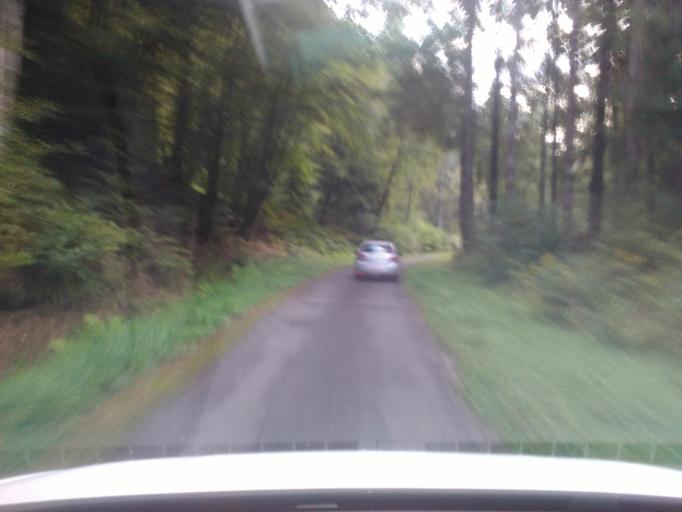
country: FR
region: Lorraine
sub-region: Departement des Vosges
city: Moyenmoutier
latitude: 48.4136
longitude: 6.9234
